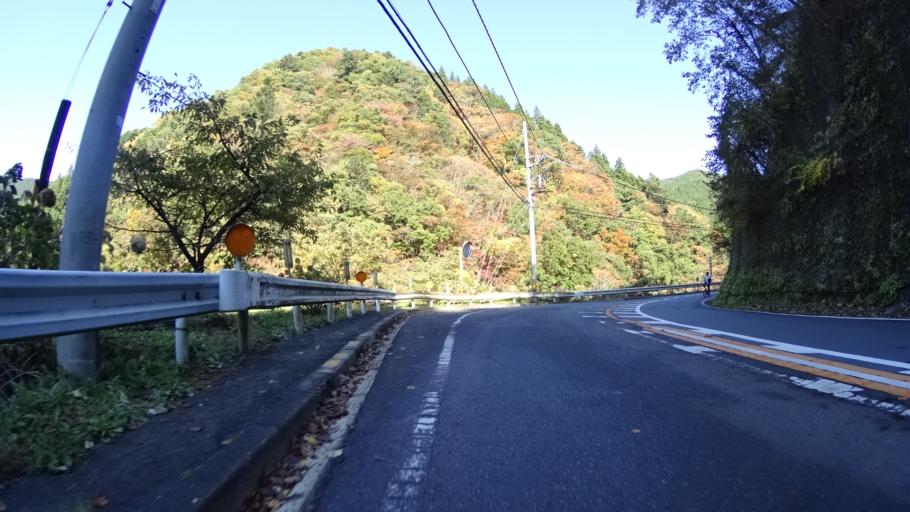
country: JP
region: Yamanashi
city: Uenohara
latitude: 35.7191
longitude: 139.0678
